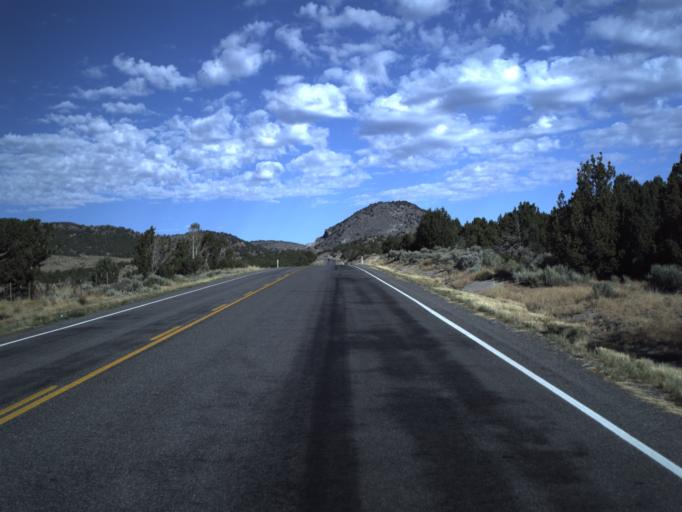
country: US
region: Utah
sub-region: Utah County
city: Genola
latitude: 39.9648
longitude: -112.0466
